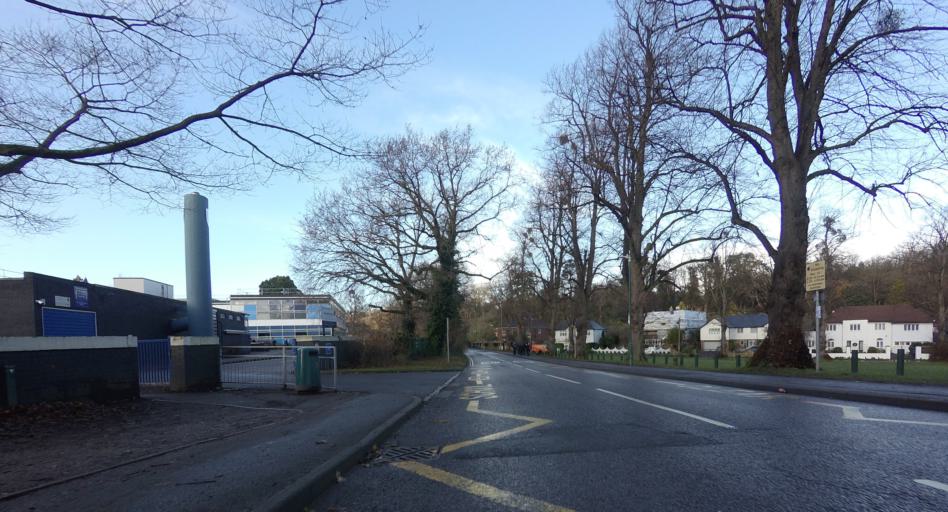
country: GB
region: England
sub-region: Kent
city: Dartford
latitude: 51.4285
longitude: 0.1953
